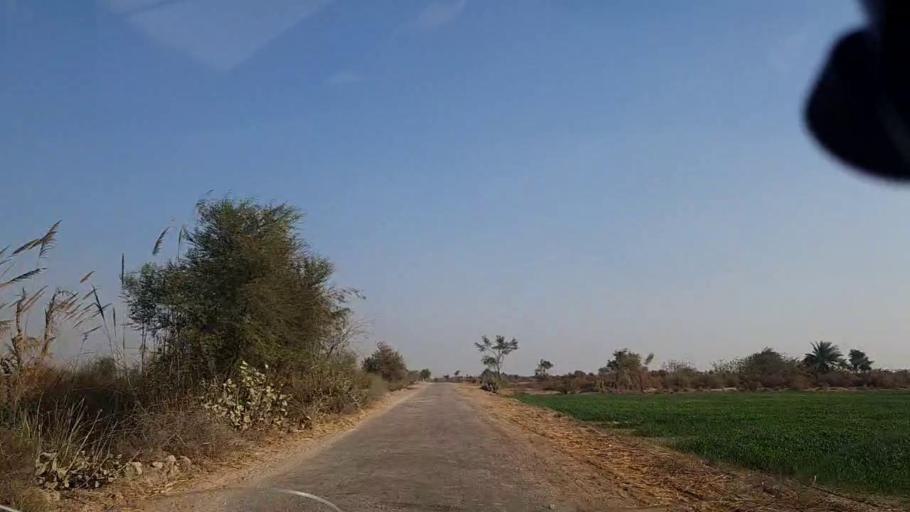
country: PK
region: Sindh
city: Khanpur
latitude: 27.6841
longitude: 69.5290
